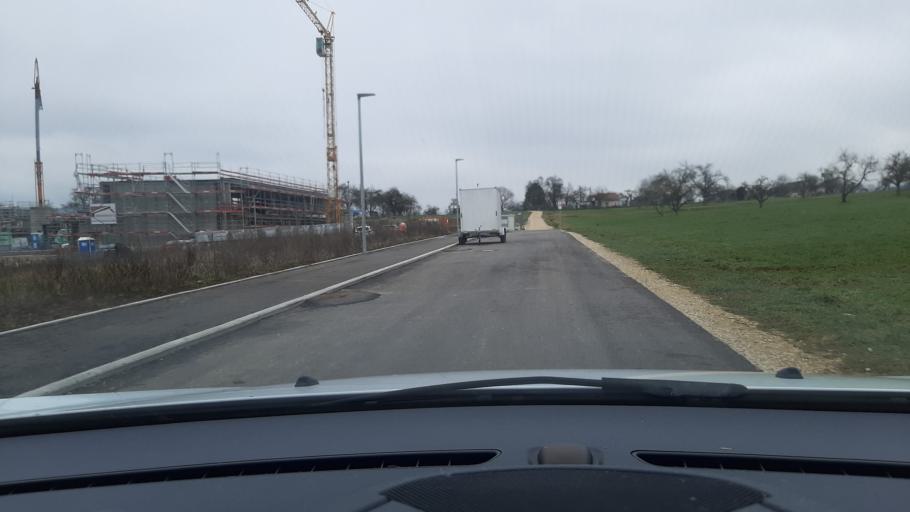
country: DE
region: Baden-Wuerttemberg
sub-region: Regierungsbezirk Stuttgart
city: Eislingen
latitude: 48.6872
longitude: 9.7079
